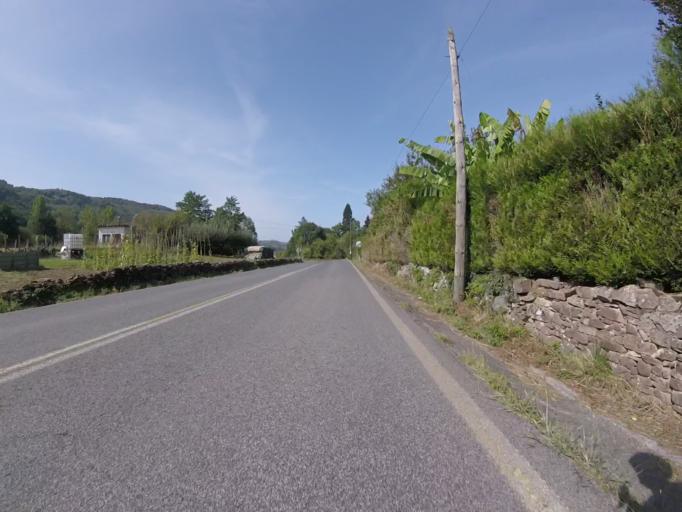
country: ES
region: Navarre
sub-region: Provincia de Navarra
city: Doneztebe
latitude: 43.1368
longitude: -1.6186
